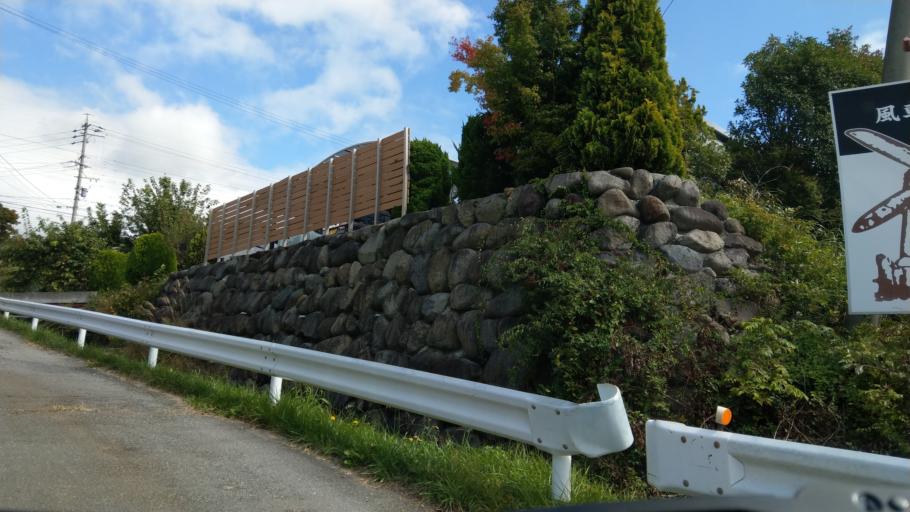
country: JP
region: Nagano
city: Komoro
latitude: 36.3341
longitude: 138.4254
